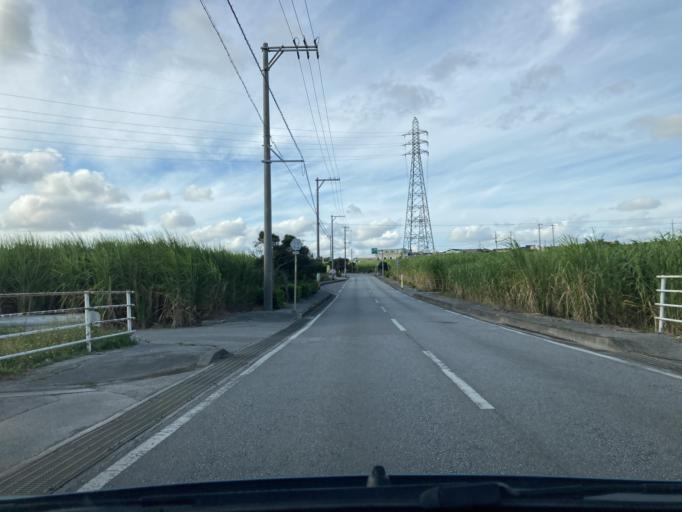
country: JP
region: Okinawa
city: Tomigusuku
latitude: 26.1556
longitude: 127.7406
